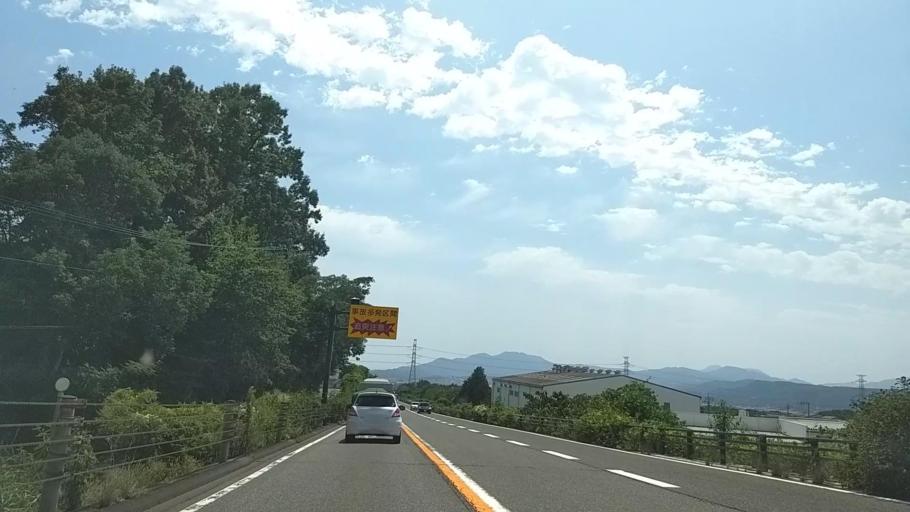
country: JP
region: Shizuoka
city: Fujinomiya
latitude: 35.2658
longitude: 138.6151
